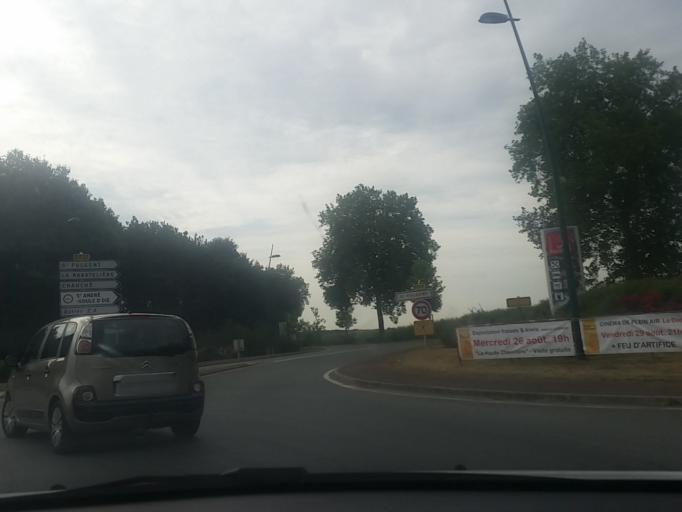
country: FR
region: Pays de la Loire
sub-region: Departement de la Vendee
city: Saint-Fulgent
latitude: 46.8637
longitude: -1.1893
